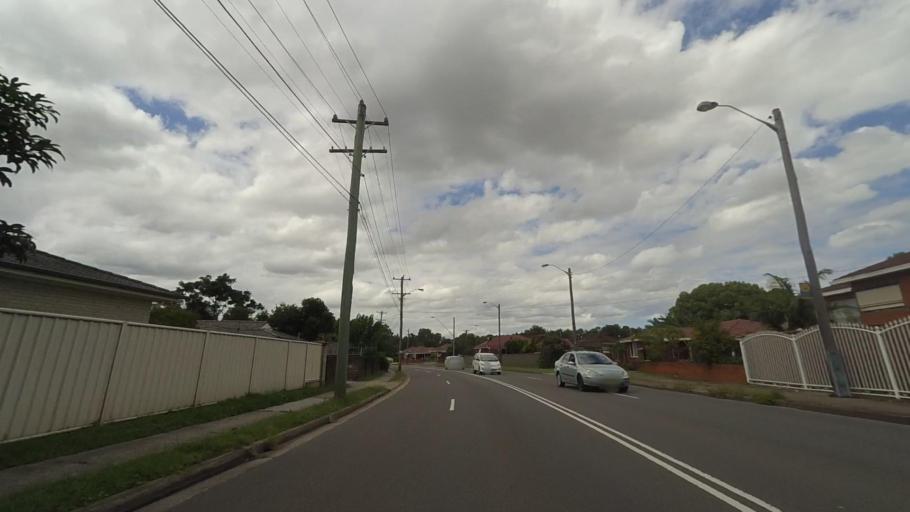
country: AU
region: New South Wales
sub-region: Fairfield
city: Fairfield East
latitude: -33.8627
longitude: 150.9567
